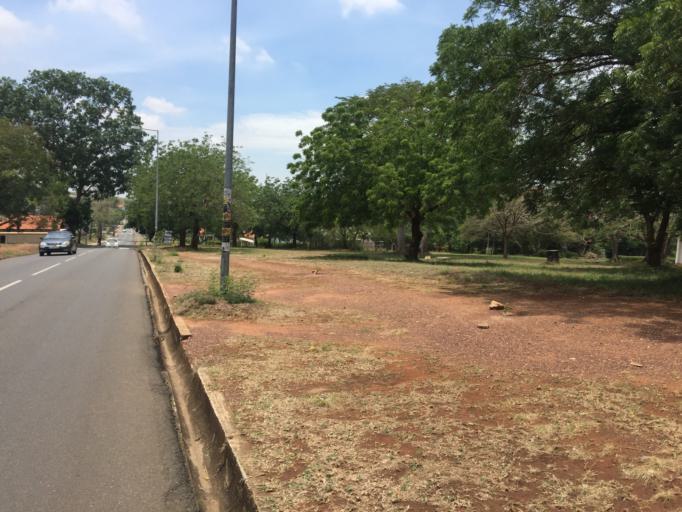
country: GH
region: Greater Accra
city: Medina Estates
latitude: 5.6533
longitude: -0.1842
